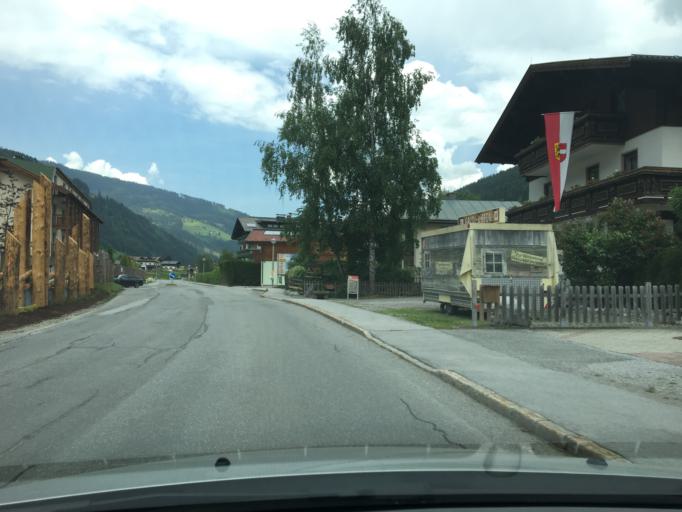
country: AT
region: Salzburg
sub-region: Politischer Bezirk Sankt Johann im Pongau
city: Kleinarl
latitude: 47.2809
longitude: 13.3175
